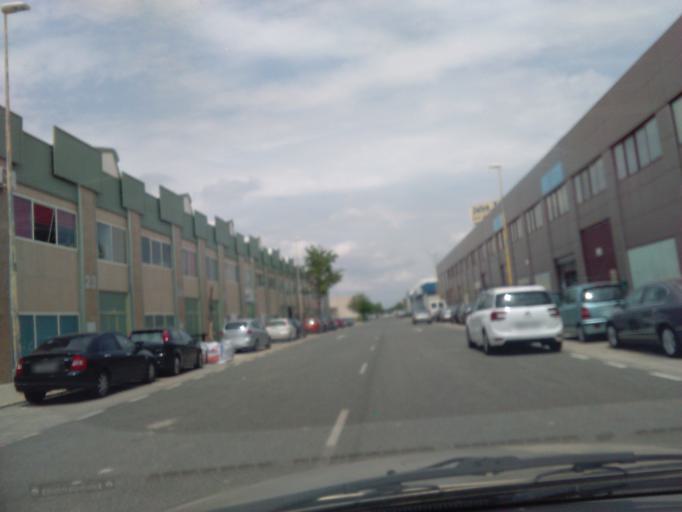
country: ES
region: Andalusia
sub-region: Provincia de Sevilla
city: Sevilla
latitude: 37.3808
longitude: -5.9328
